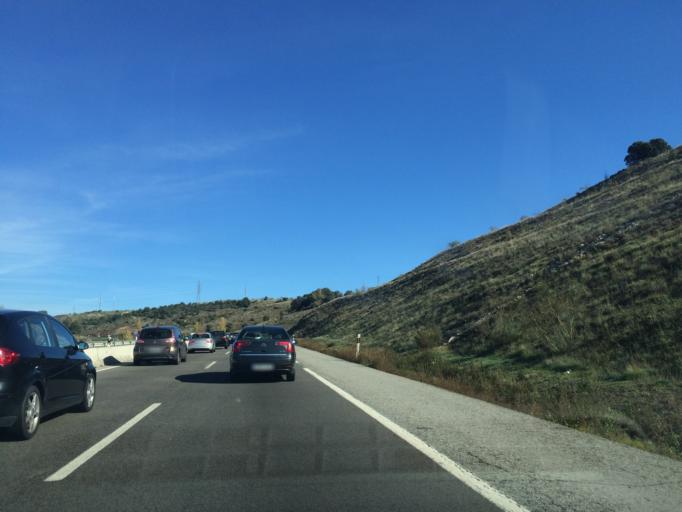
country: ES
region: Madrid
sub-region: Provincia de Madrid
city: Cabanillas de la Sierra
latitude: 40.8104
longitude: -3.6185
